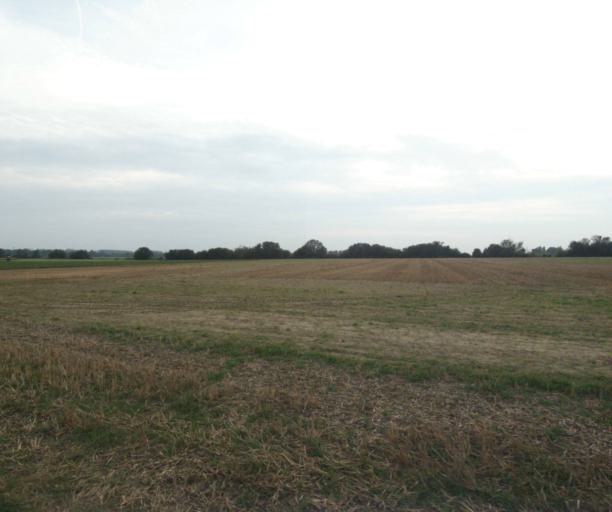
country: FR
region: Nord-Pas-de-Calais
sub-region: Departement du Nord
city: Avelin
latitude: 50.5528
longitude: 3.0709
